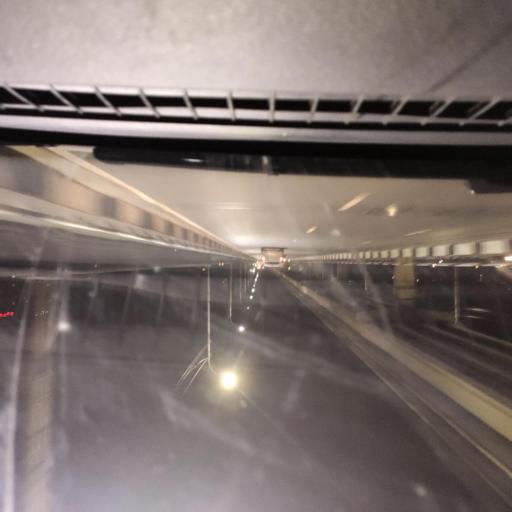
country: RU
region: Voronezj
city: Voronezh
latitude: 51.6905
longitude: 39.2444
